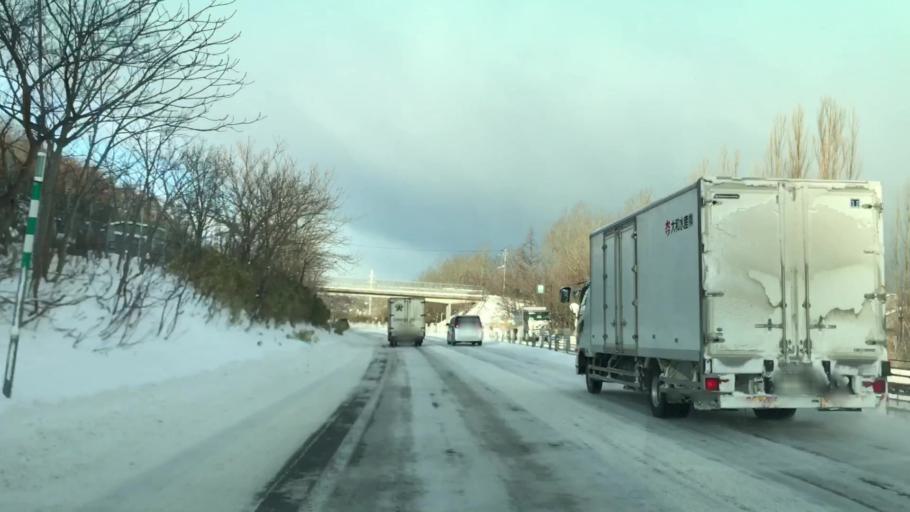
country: JP
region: Hokkaido
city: Sapporo
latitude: 43.1275
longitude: 141.1947
